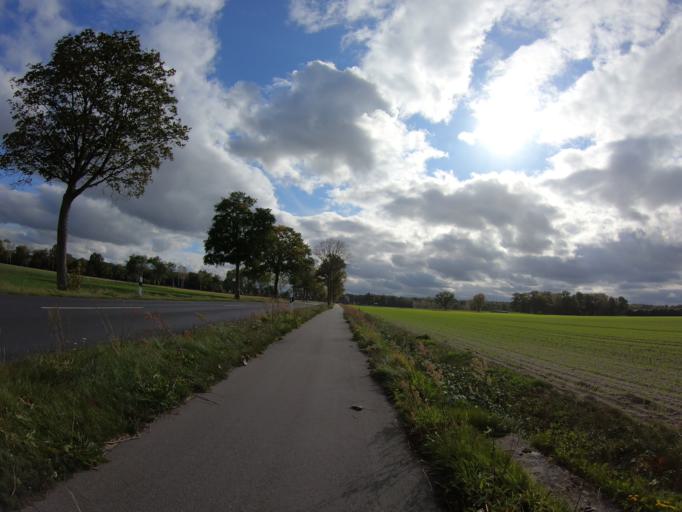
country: DE
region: Lower Saxony
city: Wasbuttel
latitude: 52.4232
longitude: 10.5895
